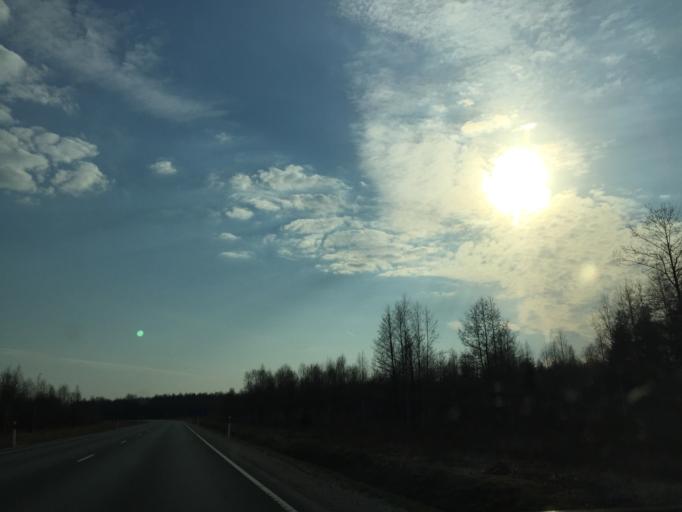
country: EE
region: Jogevamaa
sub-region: Mustvee linn
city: Mustvee
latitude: 58.8575
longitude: 26.9210
